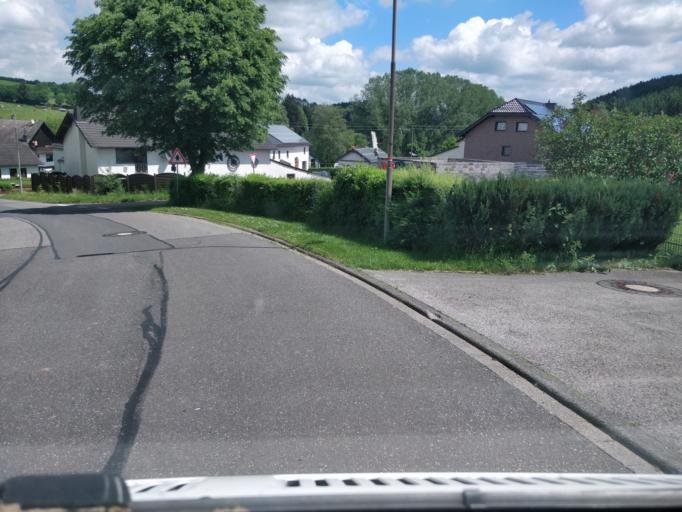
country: DE
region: Rheinland-Pfalz
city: Hallschlag
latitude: 50.3698
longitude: 6.4298
